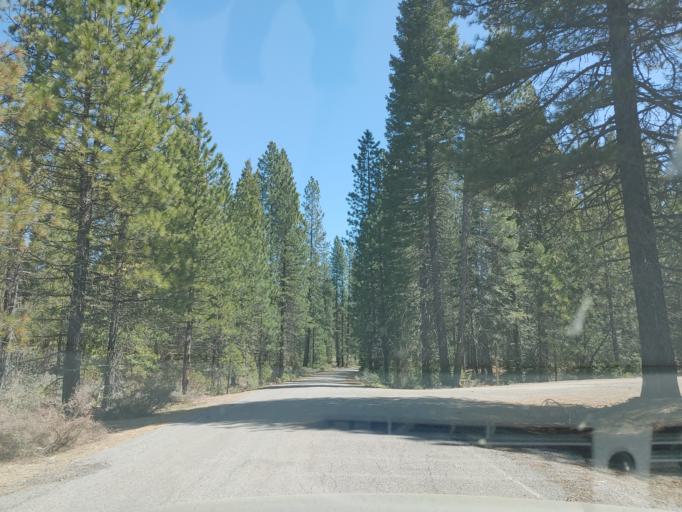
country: US
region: California
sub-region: Siskiyou County
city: McCloud
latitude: 41.2532
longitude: -121.9478
